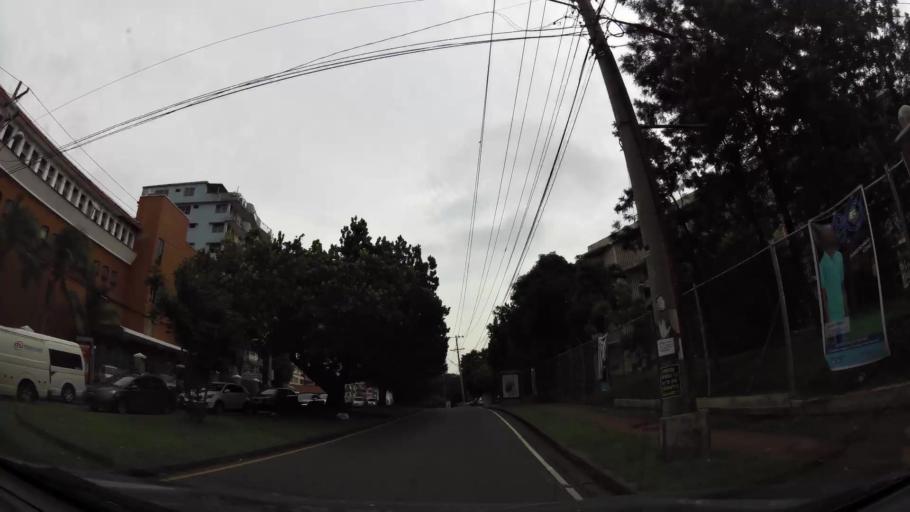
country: PA
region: Panama
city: Panama
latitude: 8.9862
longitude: -79.5317
